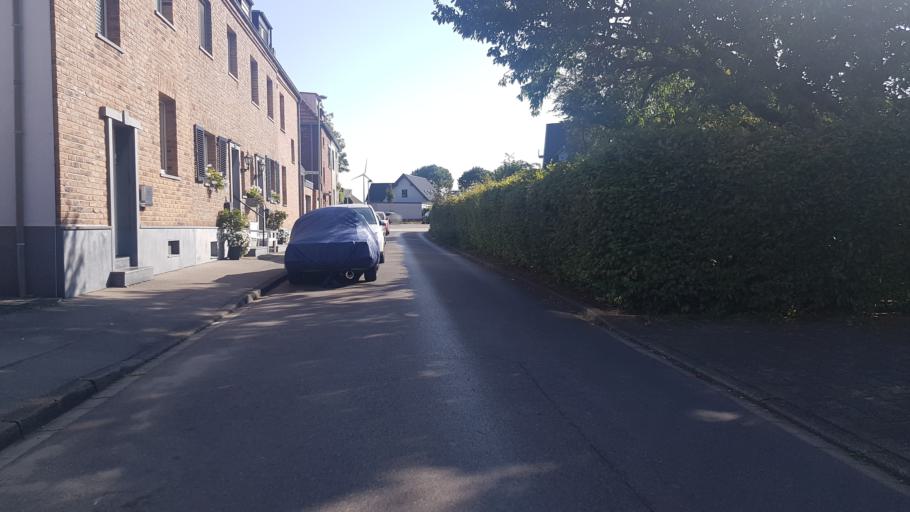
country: DE
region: North Rhine-Westphalia
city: Baesweiler
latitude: 50.9027
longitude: 6.1866
